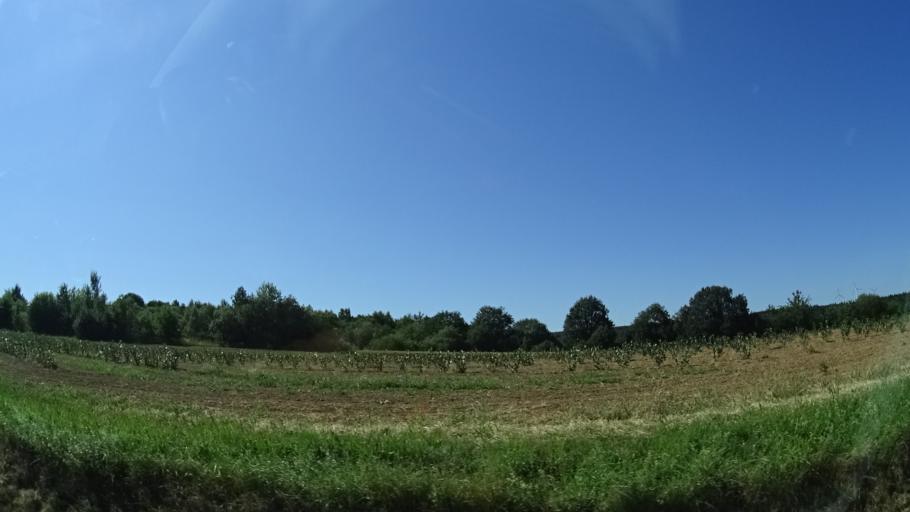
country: DE
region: Bavaria
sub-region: Regierungsbezirk Unterfranken
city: Neunkirchen
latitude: 49.7198
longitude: 9.3680
